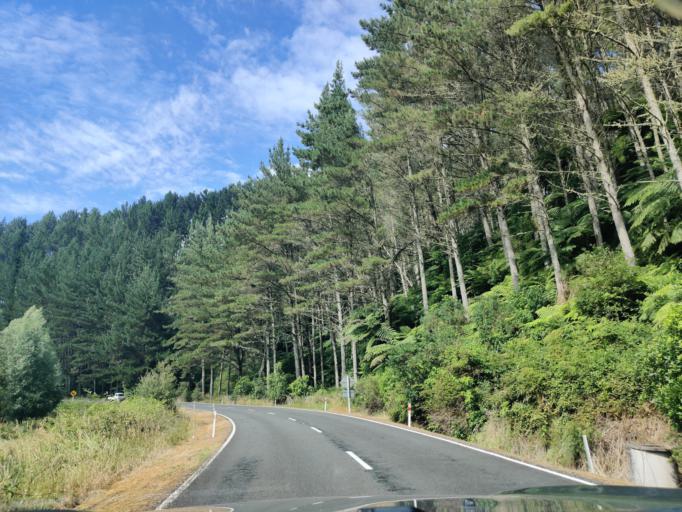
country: NZ
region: Waikato
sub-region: Otorohanga District
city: Otorohanga
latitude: -38.0990
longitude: 175.1305
